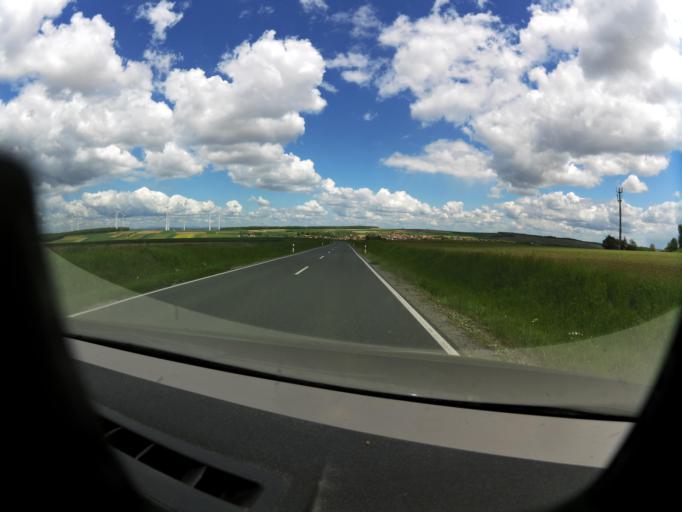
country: DE
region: Bavaria
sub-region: Regierungsbezirk Unterfranken
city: Schwanfeld
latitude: 49.9100
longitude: 10.1317
